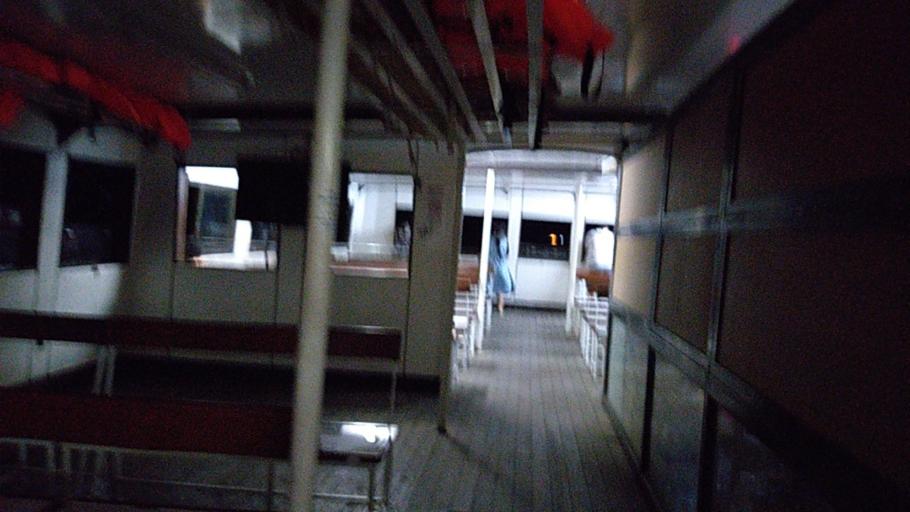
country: TH
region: Trat
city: Laem Ngop
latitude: 12.1745
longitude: 102.2982
